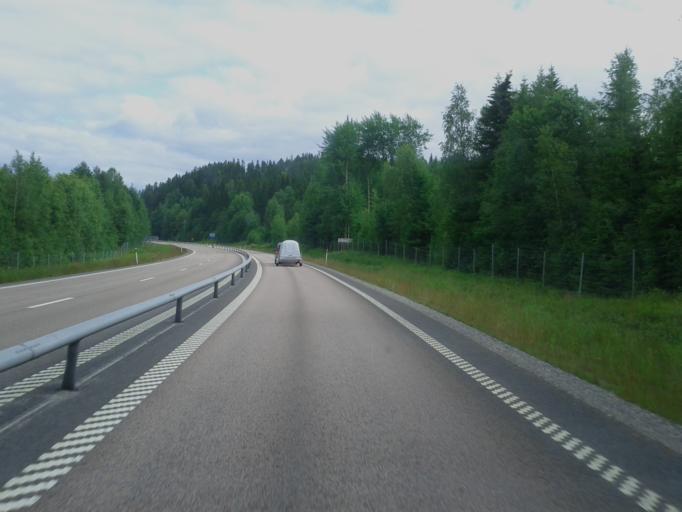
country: SE
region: Vaesternorrland
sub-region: OErnskoeldsviks Kommun
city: Bjasta
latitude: 63.2781
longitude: 18.5507
